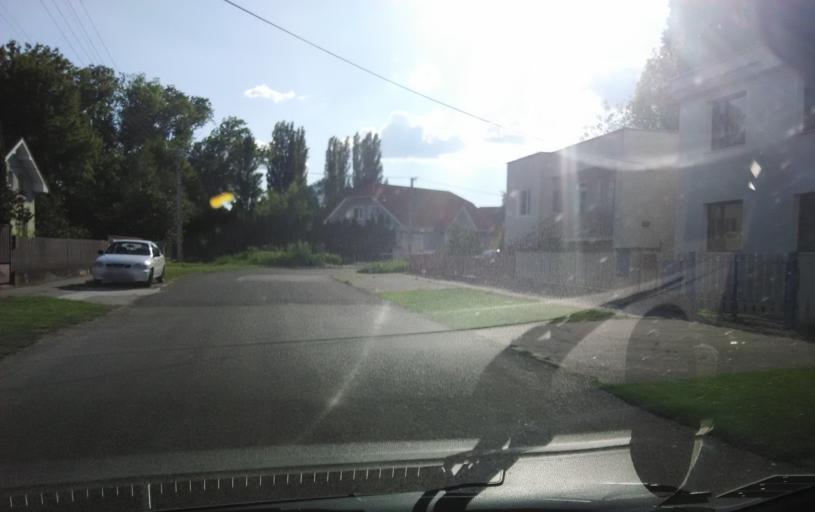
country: SK
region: Nitriansky
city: Levice
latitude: 48.2392
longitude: 18.5726
